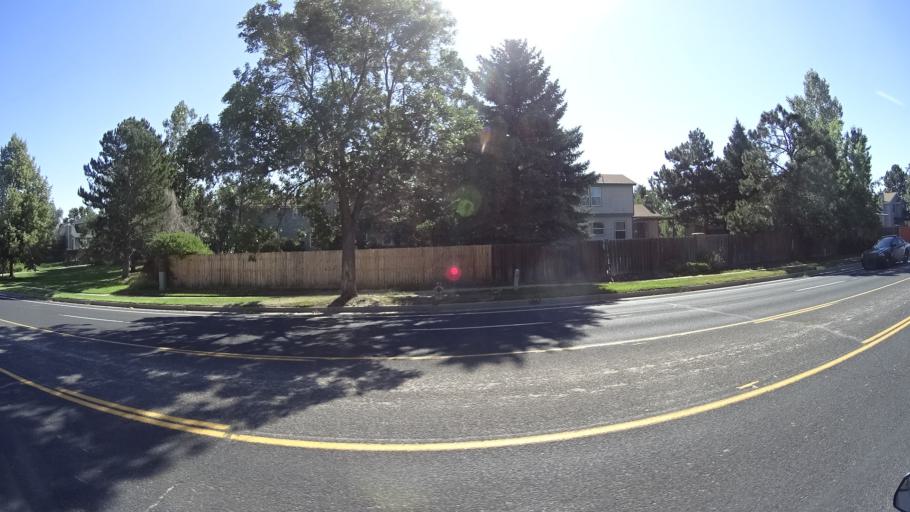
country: US
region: Colorado
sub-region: El Paso County
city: Black Forest
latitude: 38.9520
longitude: -104.7514
